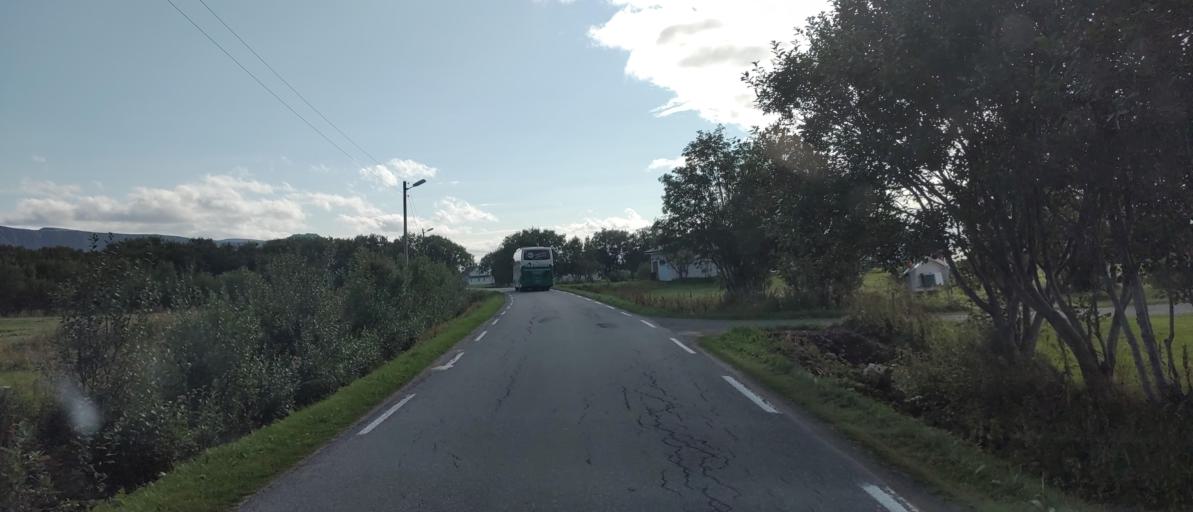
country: NO
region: Nordland
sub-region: Sortland
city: Sortland
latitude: 69.0474
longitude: 15.5172
